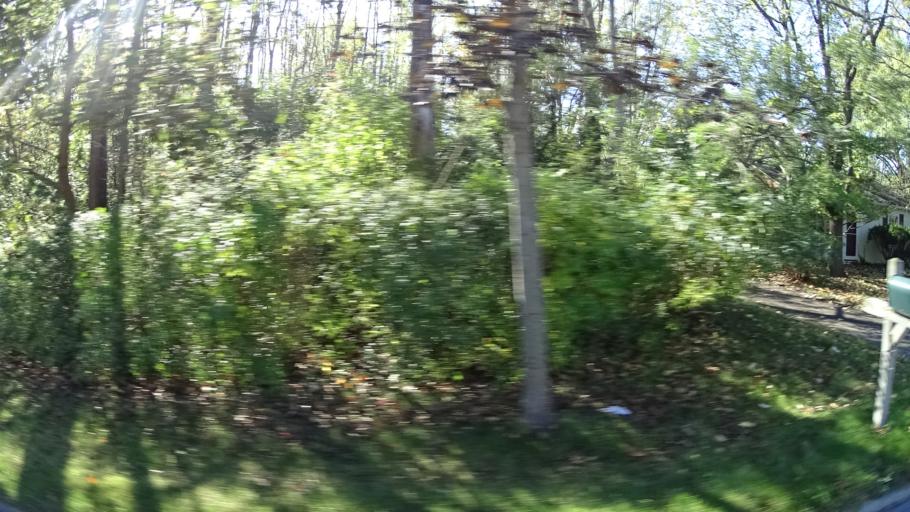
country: US
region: Ohio
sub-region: Lorain County
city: Oberlin
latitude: 41.2940
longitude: -82.2033
